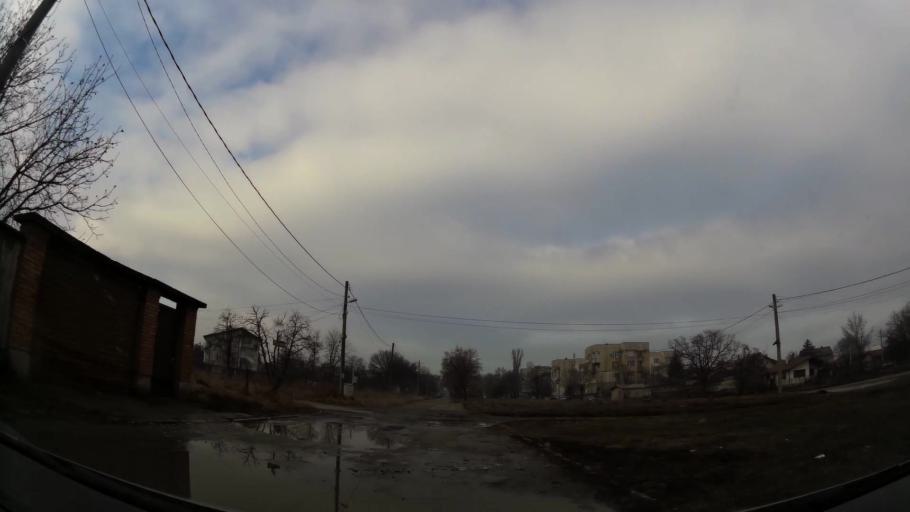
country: BG
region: Sofia-Capital
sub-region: Stolichna Obshtina
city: Sofia
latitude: 42.7374
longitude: 23.3478
